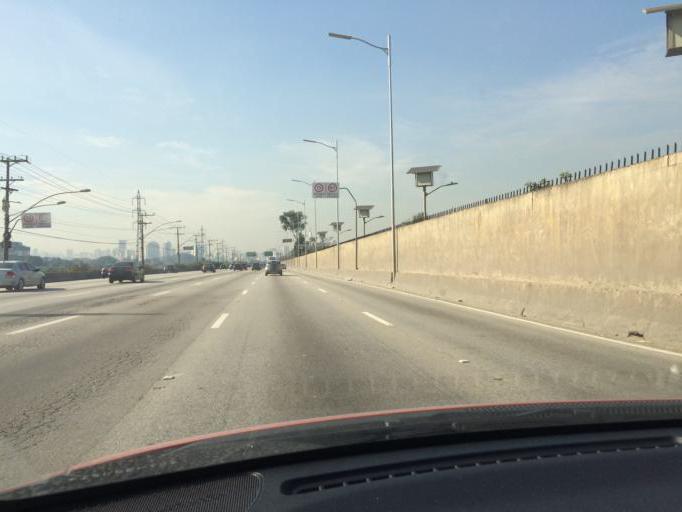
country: BR
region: Sao Paulo
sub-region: Osasco
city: Osasco
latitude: -23.5544
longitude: -46.7218
